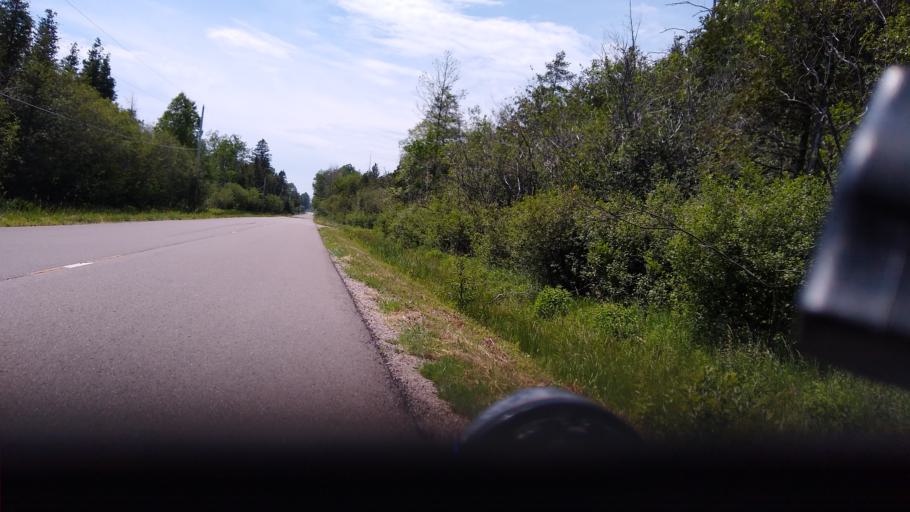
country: US
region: Michigan
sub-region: Delta County
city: Escanaba
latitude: 45.7100
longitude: -87.1103
